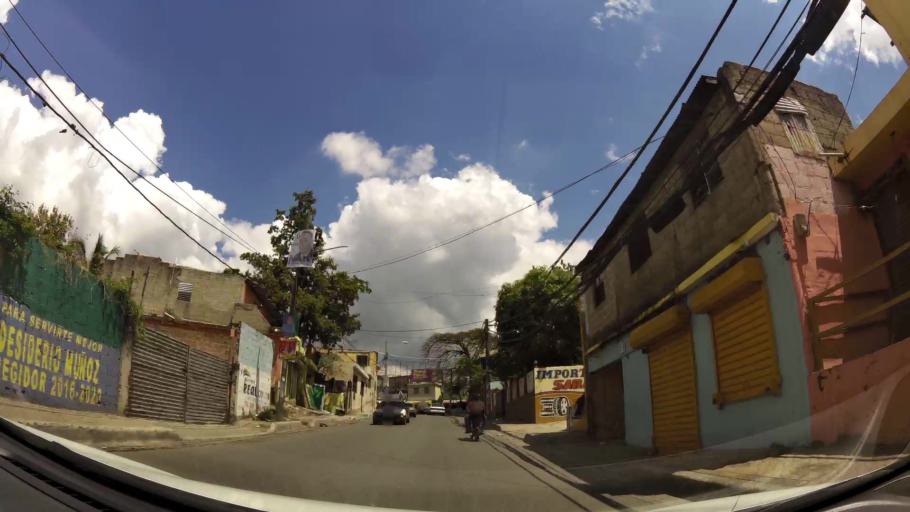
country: DO
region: Santo Domingo
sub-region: Santo Domingo
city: Santo Domingo Este
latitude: 18.5386
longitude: -69.8619
